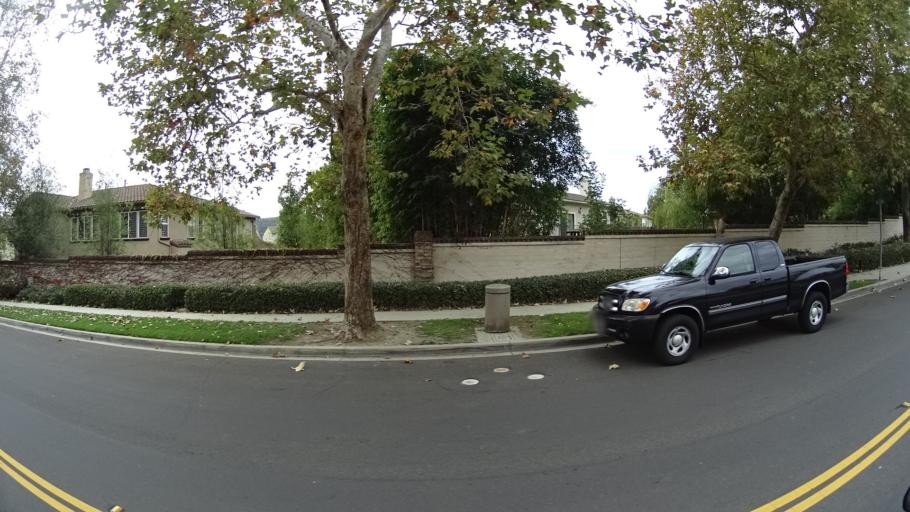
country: US
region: California
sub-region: Orange County
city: Aliso Viejo
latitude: 33.5681
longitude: -117.7390
